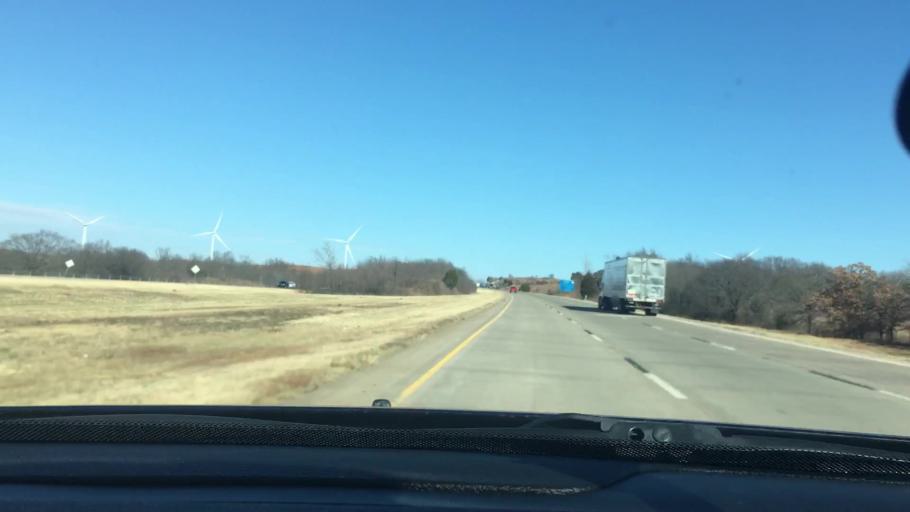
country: US
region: Oklahoma
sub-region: Murray County
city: Davis
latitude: 34.3618
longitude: -97.1476
